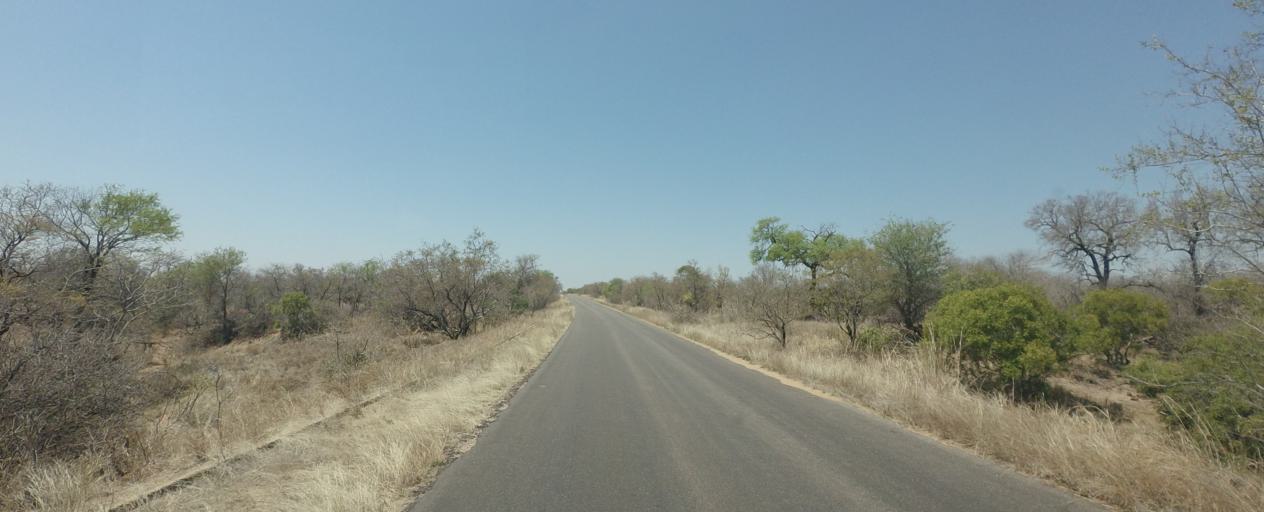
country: ZA
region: Limpopo
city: Thulamahashi
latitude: -24.4723
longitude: 31.4274
